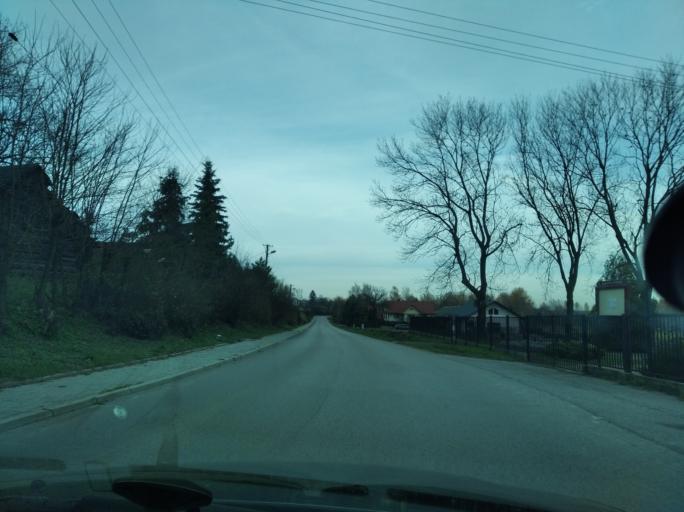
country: PL
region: Subcarpathian Voivodeship
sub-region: Powiat przeworski
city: Debow
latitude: 50.0452
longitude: 22.4587
